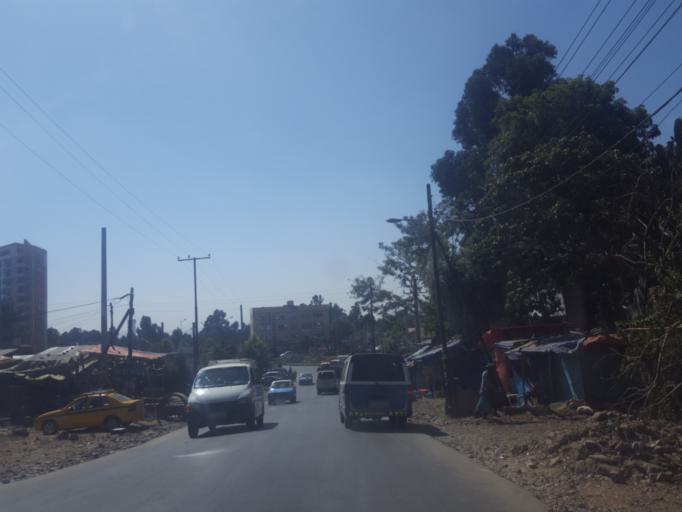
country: ET
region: Adis Abeba
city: Addis Ababa
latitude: 9.0504
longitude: 38.7376
